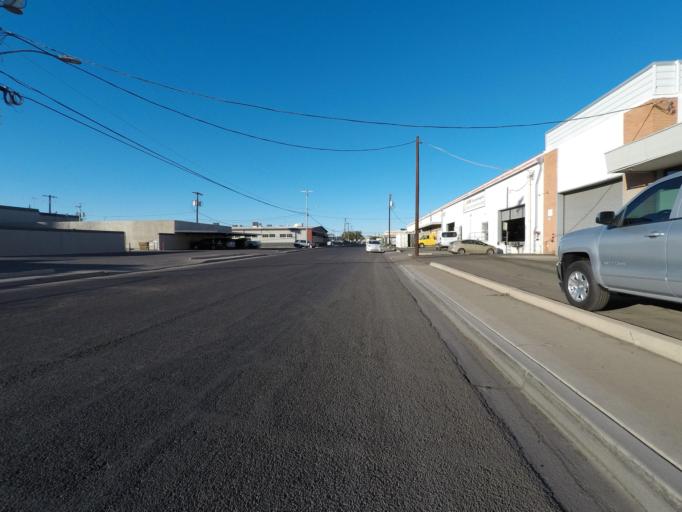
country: US
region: Arizona
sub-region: Maricopa County
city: Phoenix
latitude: 33.4689
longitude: -112.1063
